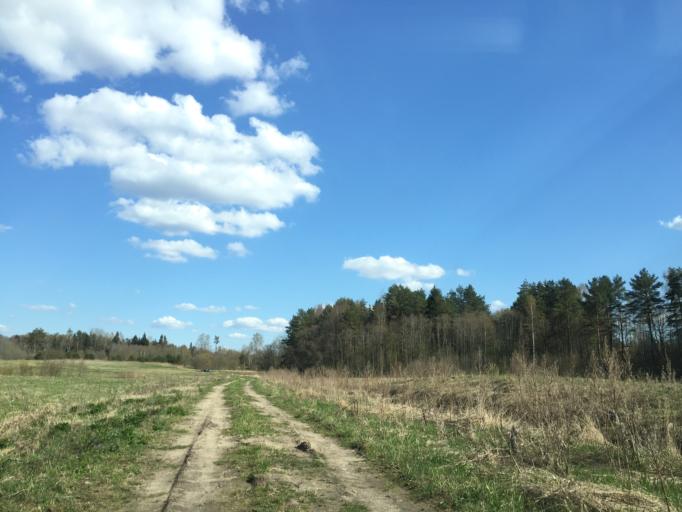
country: LV
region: Krimulda
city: Ragana
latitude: 57.3433
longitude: 24.6937
